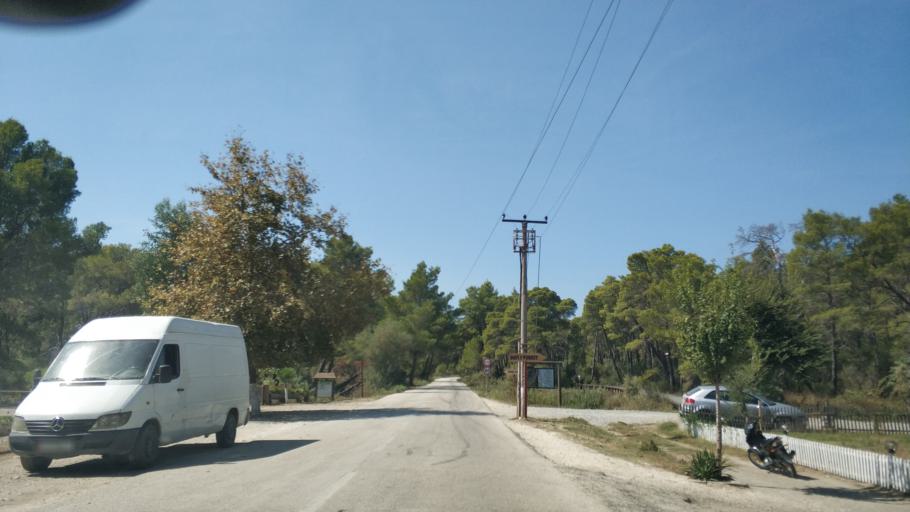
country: AL
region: Fier
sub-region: Rrethi i Lushnjes
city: Divjake
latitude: 40.9902
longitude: 19.4969
